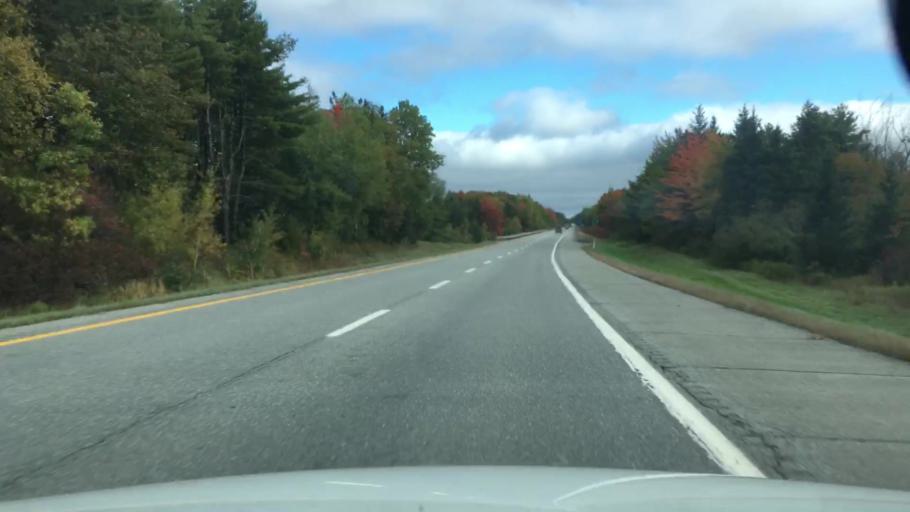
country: US
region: Maine
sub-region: Penobscot County
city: Carmel
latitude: 44.7695
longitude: -69.0005
